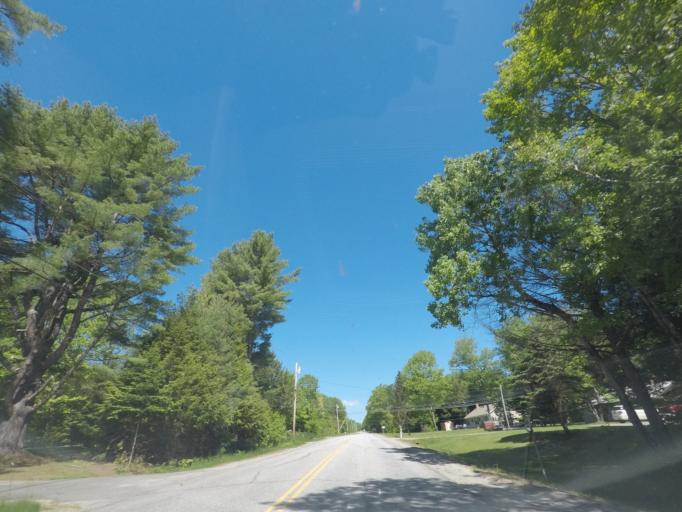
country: US
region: Maine
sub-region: Kennebec County
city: Manchester
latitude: 44.2309
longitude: -69.8808
